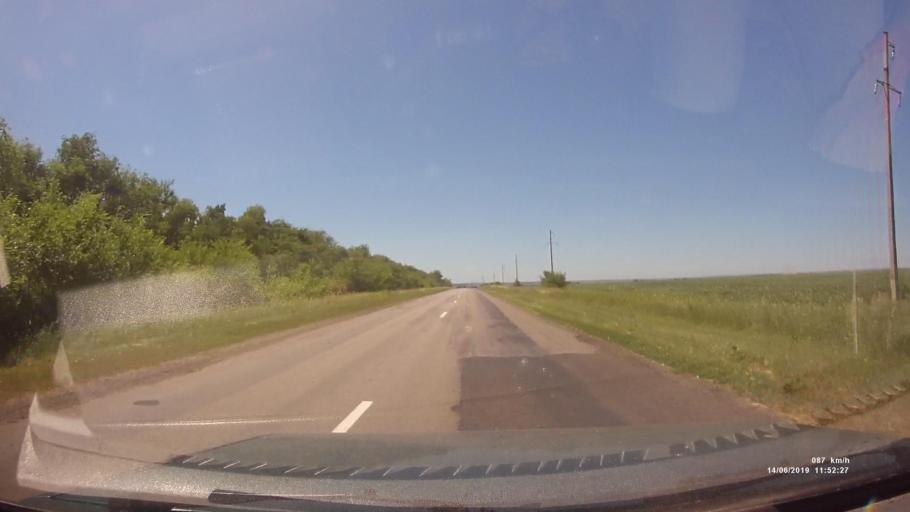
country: RU
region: Rostov
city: Kazanskaya
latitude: 49.8357
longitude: 41.2284
